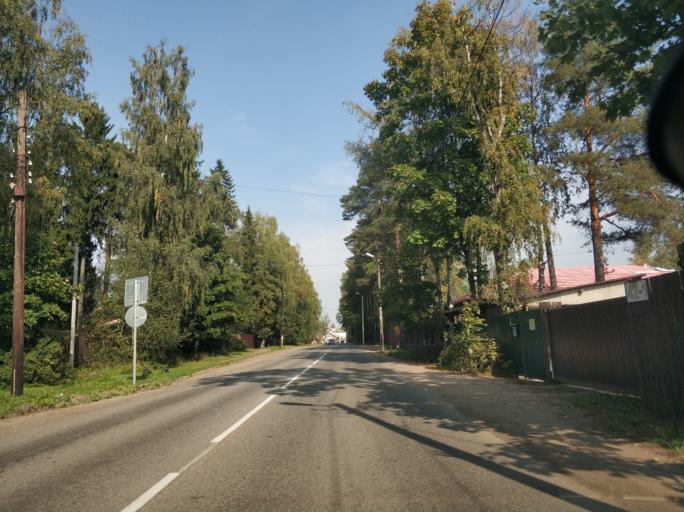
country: RU
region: Leningrad
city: Vsevolozhsk
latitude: 60.0134
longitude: 30.6215
